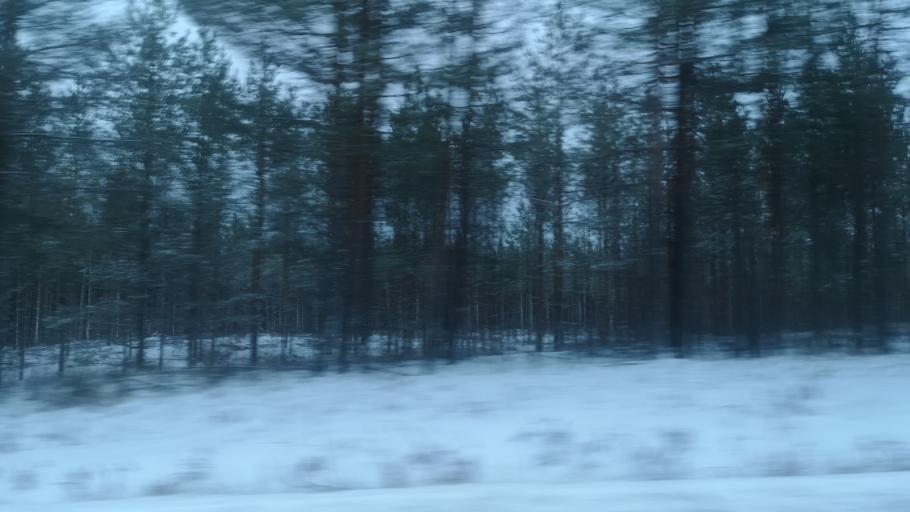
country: FI
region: Southern Savonia
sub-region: Savonlinna
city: Enonkoski
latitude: 62.0995
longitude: 28.6578
